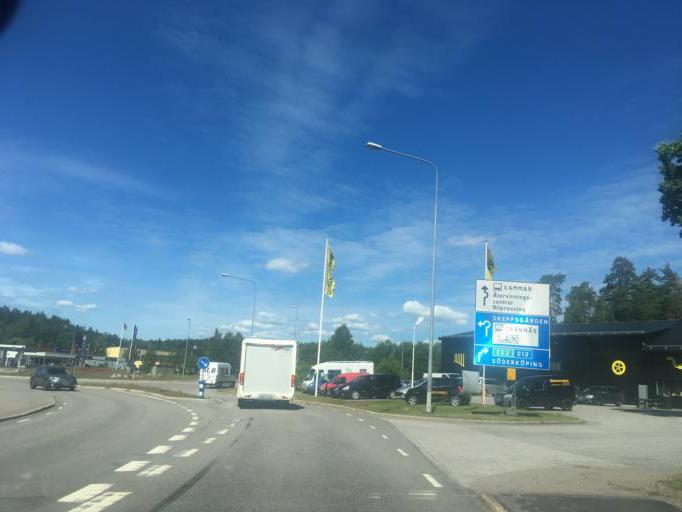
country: SE
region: OEstergoetland
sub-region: Valdemarsviks Kommun
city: Valdemarsvik
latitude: 58.2117
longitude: 16.5855
